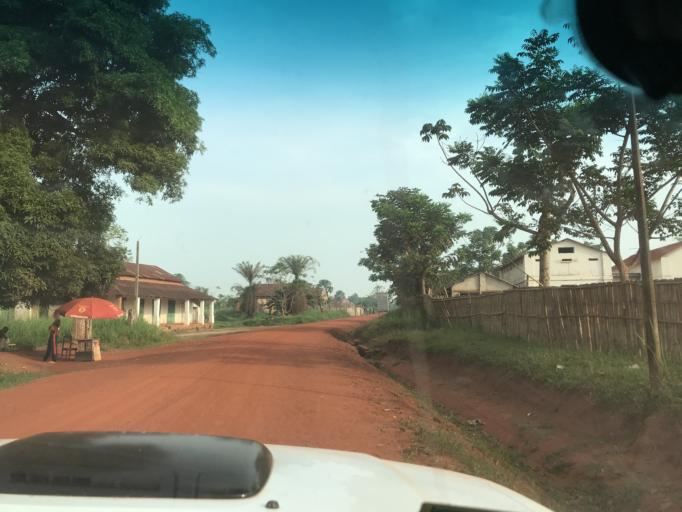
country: CD
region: Eastern Province
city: Buta
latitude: 2.7912
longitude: 24.7265
